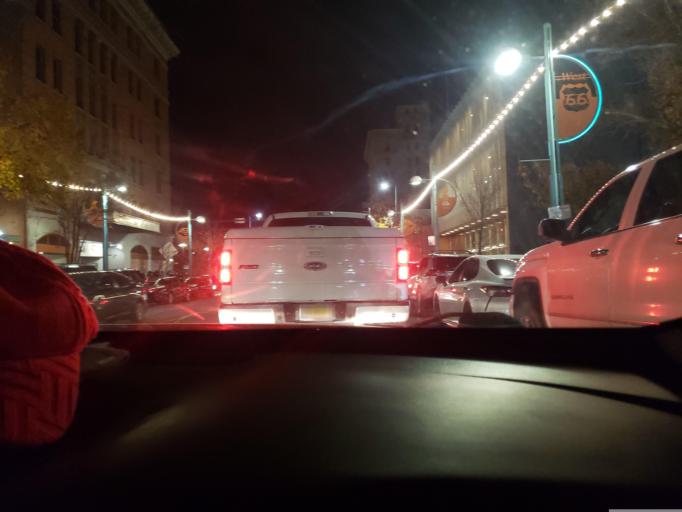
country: US
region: New Mexico
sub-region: Bernalillo County
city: Albuquerque
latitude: 35.0842
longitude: -106.6486
